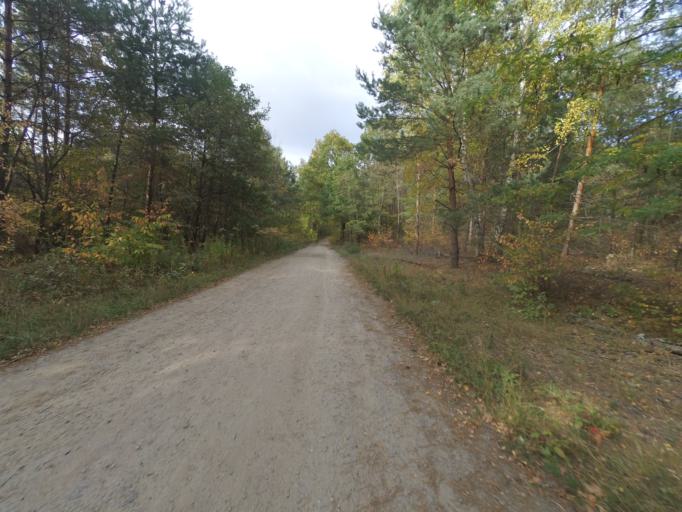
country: DE
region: Saxony
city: Albertstadt
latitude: 51.0848
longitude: 13.7838
